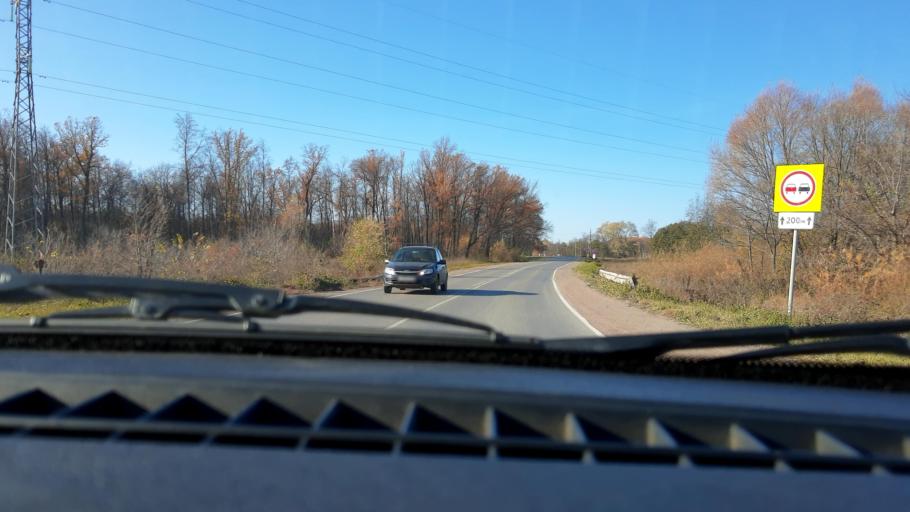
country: RU
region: Bashkortostan
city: Mikhaylovka
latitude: 54.8047
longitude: 55.8246
